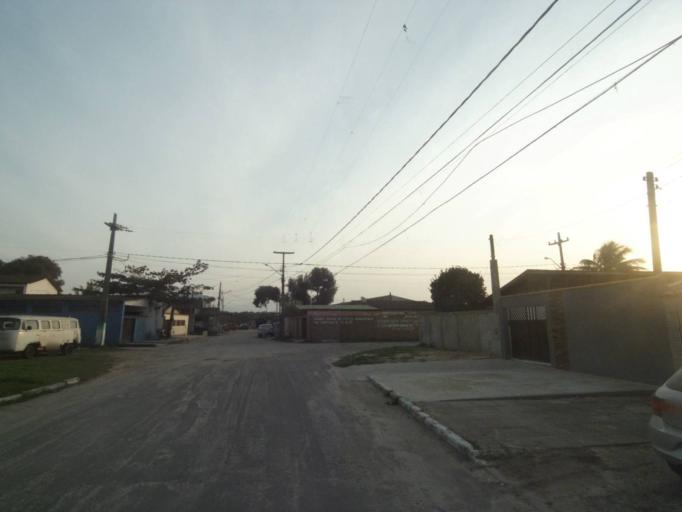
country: BR
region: Parana
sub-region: Paranagua
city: Paranagua
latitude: -25.5167
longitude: -48.5464
